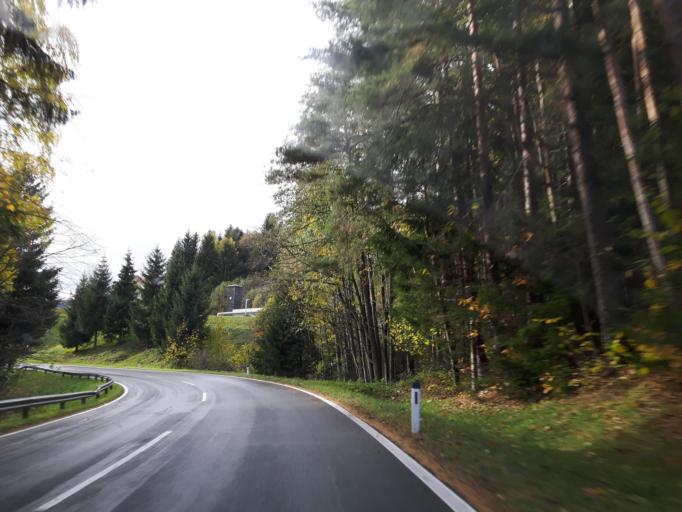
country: AT
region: Styria
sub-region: Politischer Bezirk Deutschlandsberg
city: Sankt Oswald ob Eibiswald
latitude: 46.7091
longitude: 15.1502
